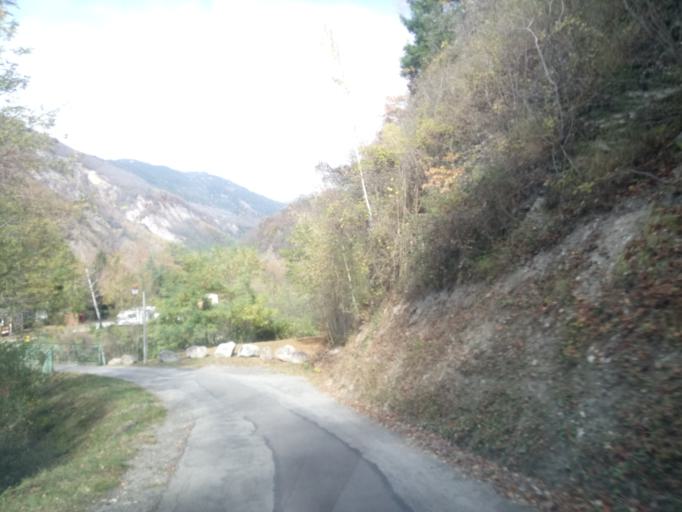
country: FR
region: Rhone-Alpes
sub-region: Departement de la Savoie
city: La Chambre
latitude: 45.3683
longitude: 6.3148
